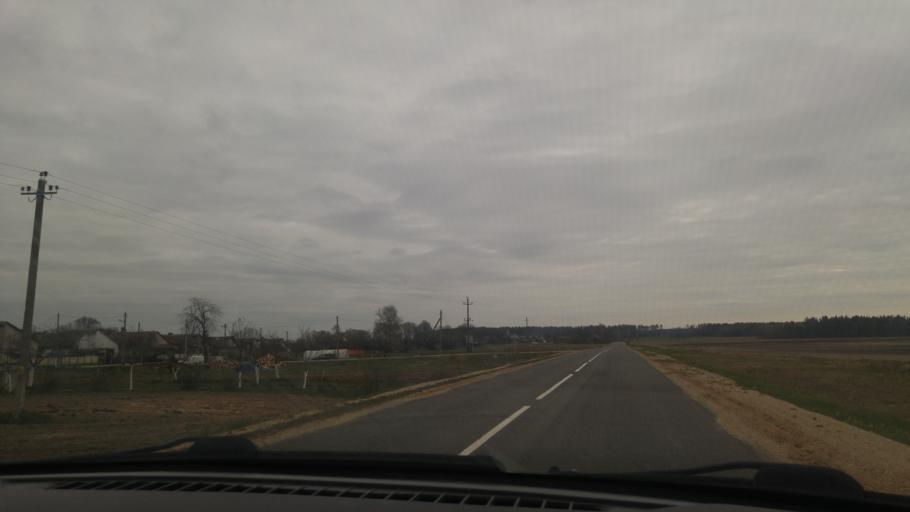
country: BY
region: Minsk
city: Chervyen'
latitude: 53.7262
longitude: 28.2693
